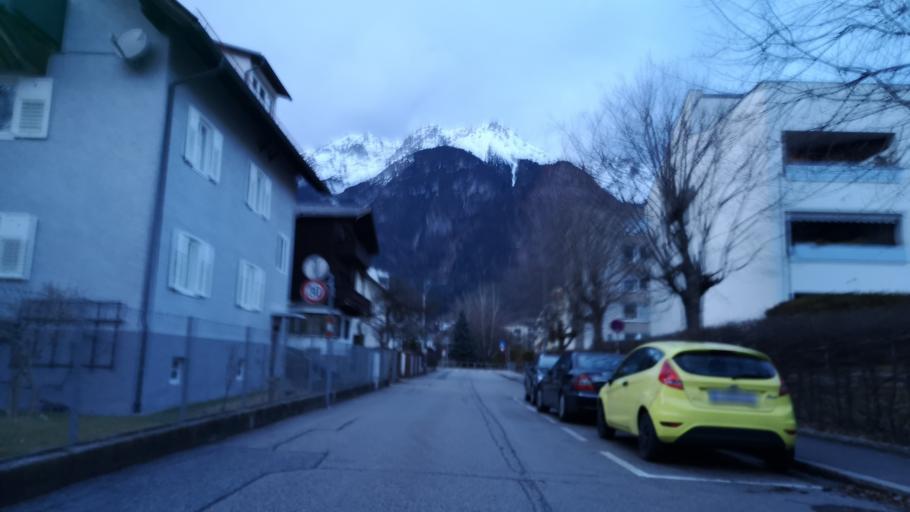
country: AT
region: Tyrol
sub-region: Politischer Bezirk Innsbruck Land
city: Natters
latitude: 47.2563
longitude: 11.3677
